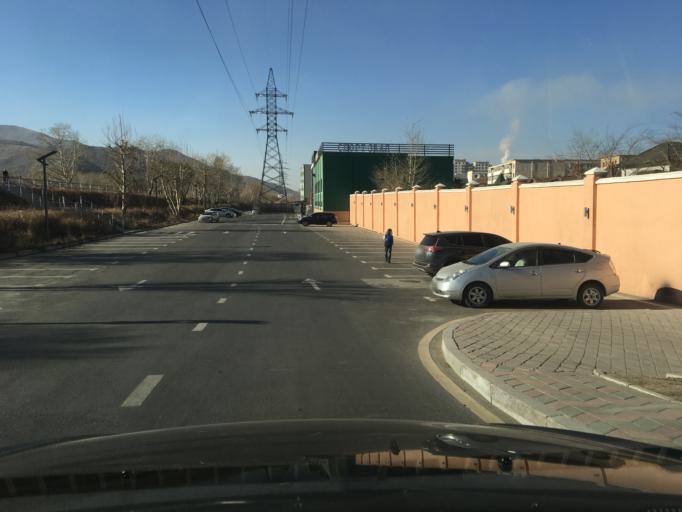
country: MN
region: Ulaanbaatar
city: Ulaanbaatar
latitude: 47.8909
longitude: 106.9091
